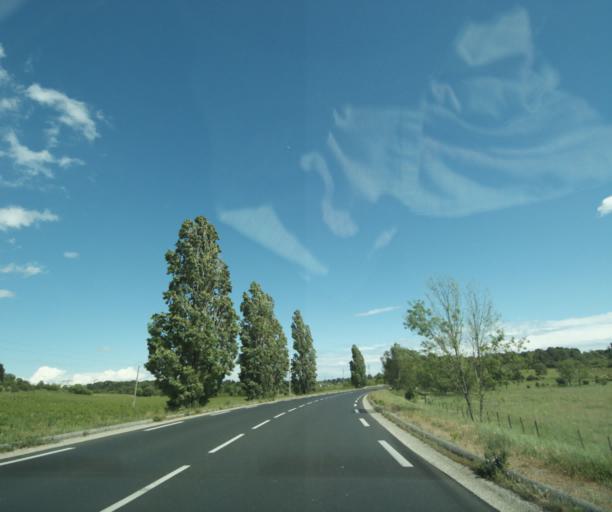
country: FR
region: Languedoc-Roussillon
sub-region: Departement de l'Herault
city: Saint-Jean-de-Vedas
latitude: 43.5874
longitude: 3.8341
